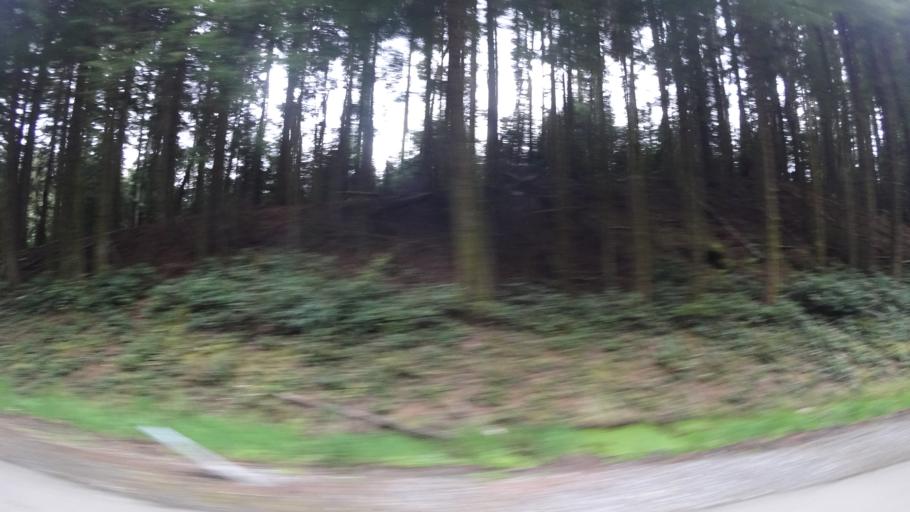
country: US
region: Oregon
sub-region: Coos County
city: Barview
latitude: 43.2425
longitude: -124.2881
